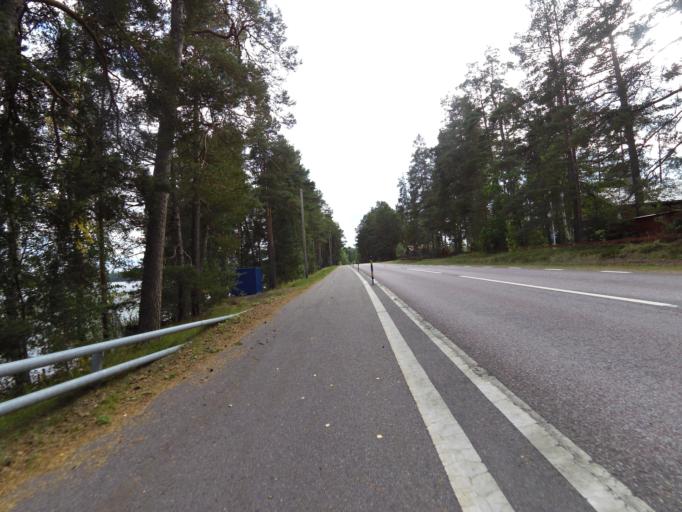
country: SE
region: Gaevleborg
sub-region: Sandvikens Kommun
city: Sandviken
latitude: 60.6962
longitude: 16.8166
